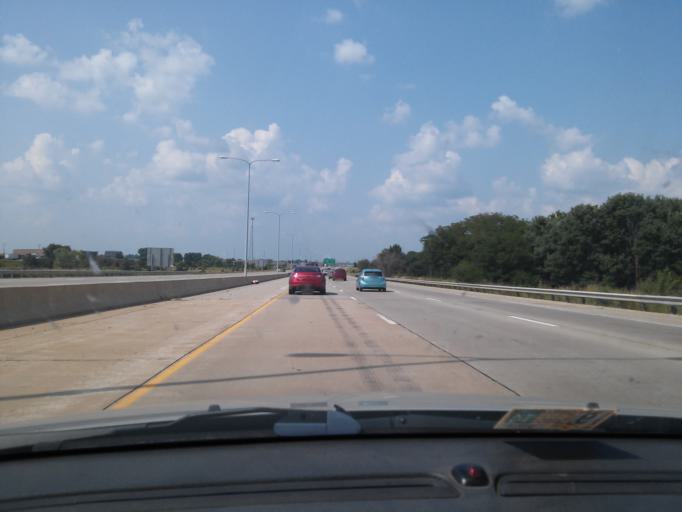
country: US
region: Illinois
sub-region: McLean County
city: Normal
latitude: 40.5098
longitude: -89.0287
